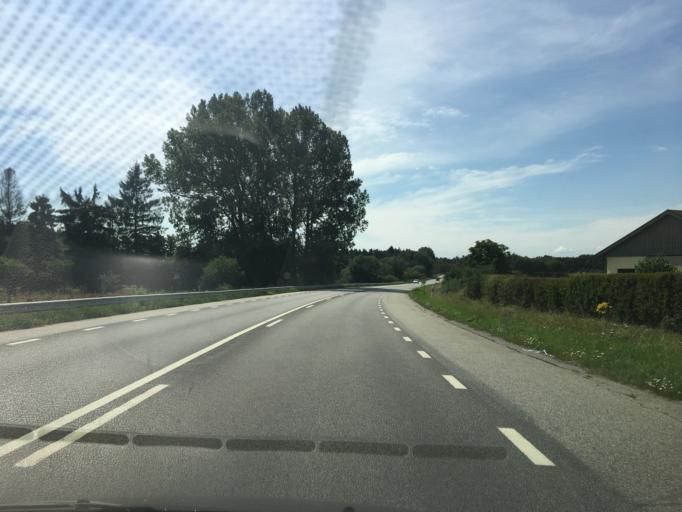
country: SE
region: Skane
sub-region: Kavlinge Kommun
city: Hofterup
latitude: 55.8320
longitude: 12.9600
